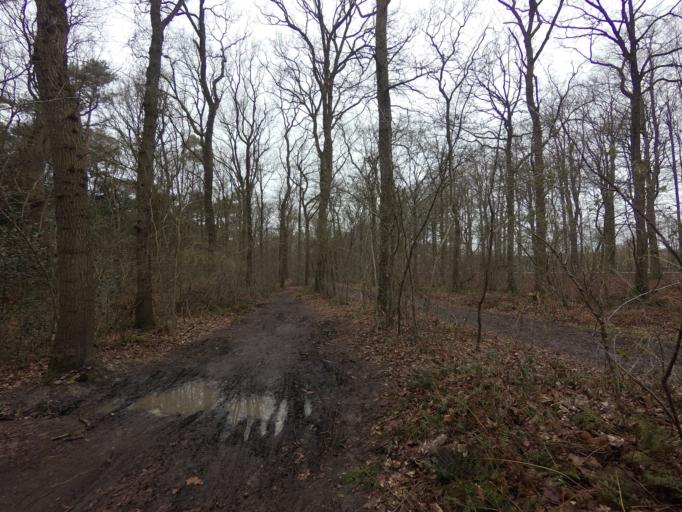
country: NL
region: Friesland
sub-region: Gemeente Gaasterlan-Sleat
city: Oudemirdum
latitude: 52.8694
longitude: 5.5408
